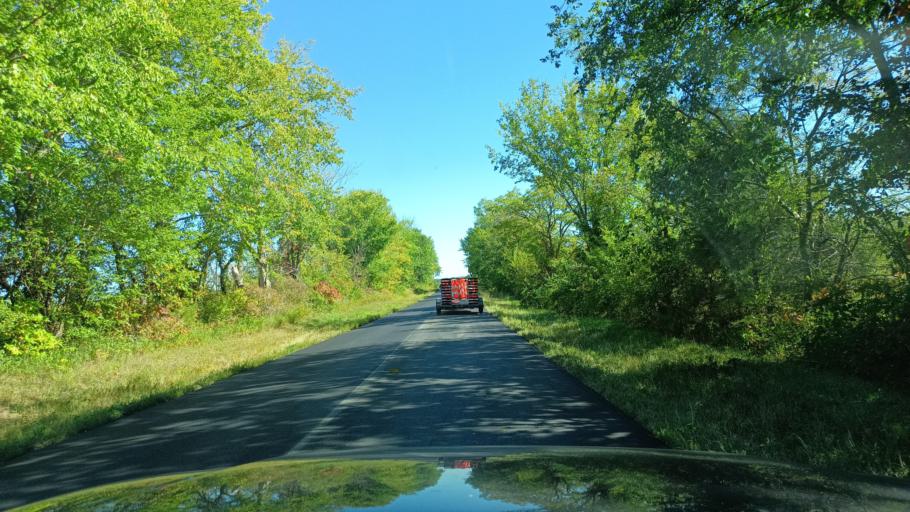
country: US
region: Missouri
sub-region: Macon County
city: La Plata
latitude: 39.9238
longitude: -92.5346
